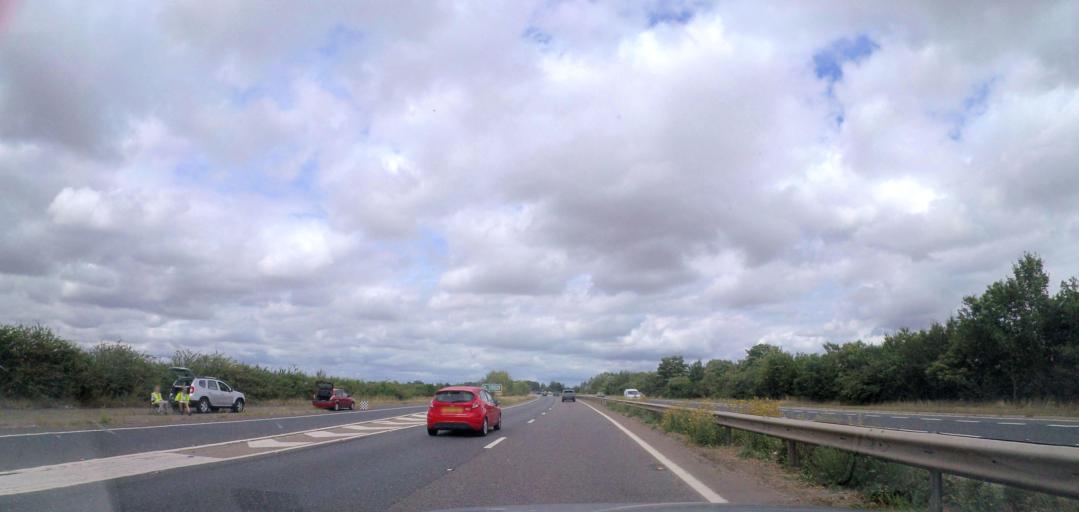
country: GB
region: England
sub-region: Cambridgeshire
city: Balsham
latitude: 52.1793
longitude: 0.2957
